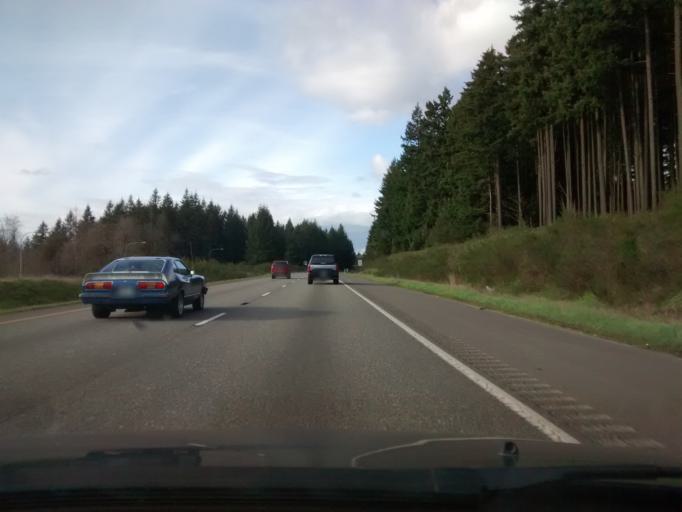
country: US
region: Washington
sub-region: Kitsap County
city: Burley
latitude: 47.4216
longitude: -122.6230
